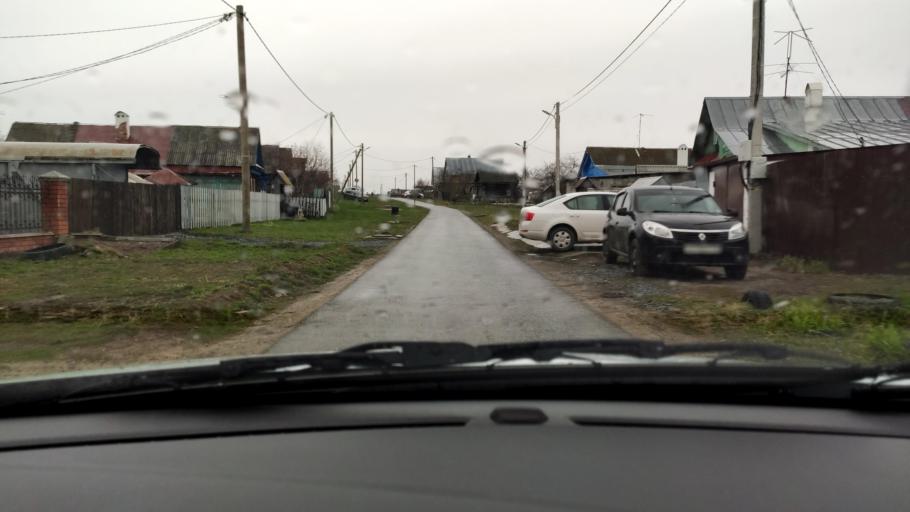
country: RU
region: Tatarstan
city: Osinovo
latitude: 55.8299
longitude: 48.8617
